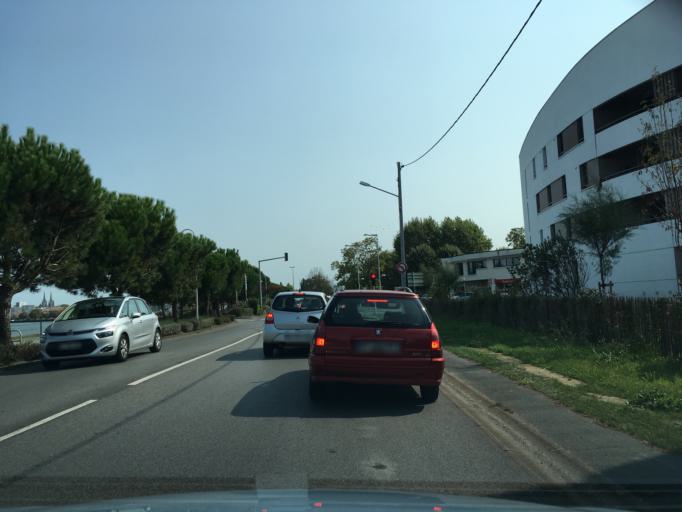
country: FR
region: Aquitaine
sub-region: Departement des Pyrenees-Atlantiques
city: Bayonne
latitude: 43.5046
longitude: -1.4955
